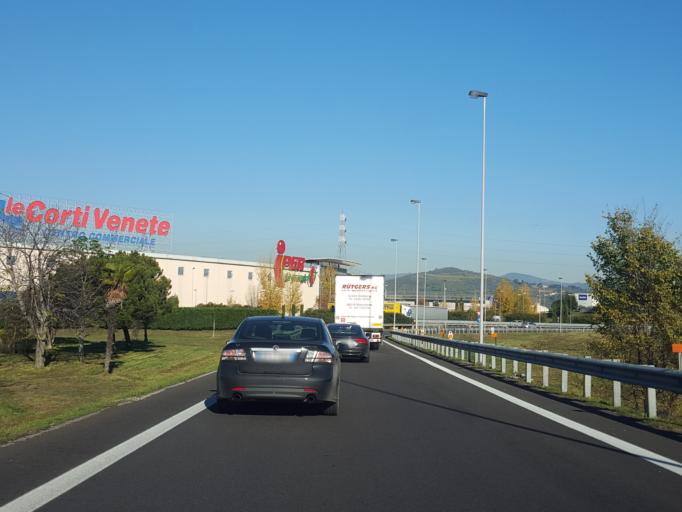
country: IT
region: Veneto
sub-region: Provincia di Verona
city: San Martino Buon Albergo
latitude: 45.4104
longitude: 11.0936
